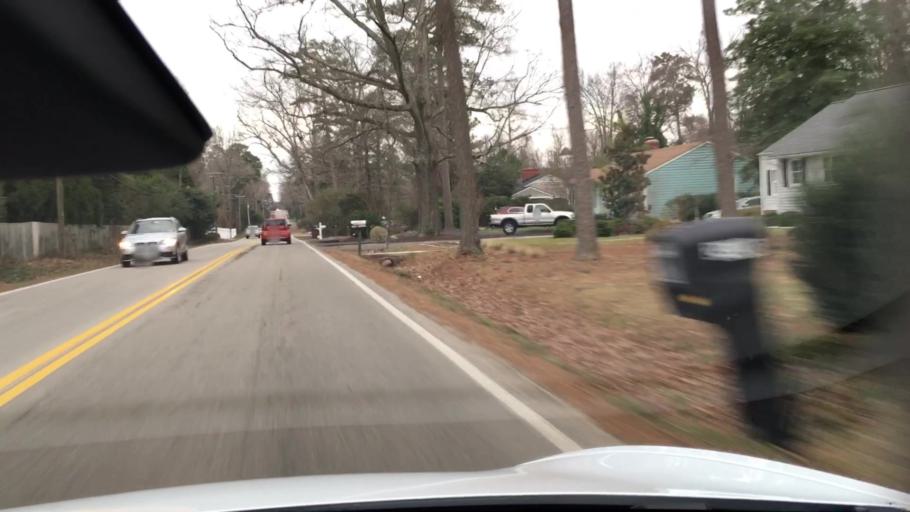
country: US
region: Virginia
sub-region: Chesterfield County
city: Bon Air
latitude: 37.5318
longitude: -77.5604
